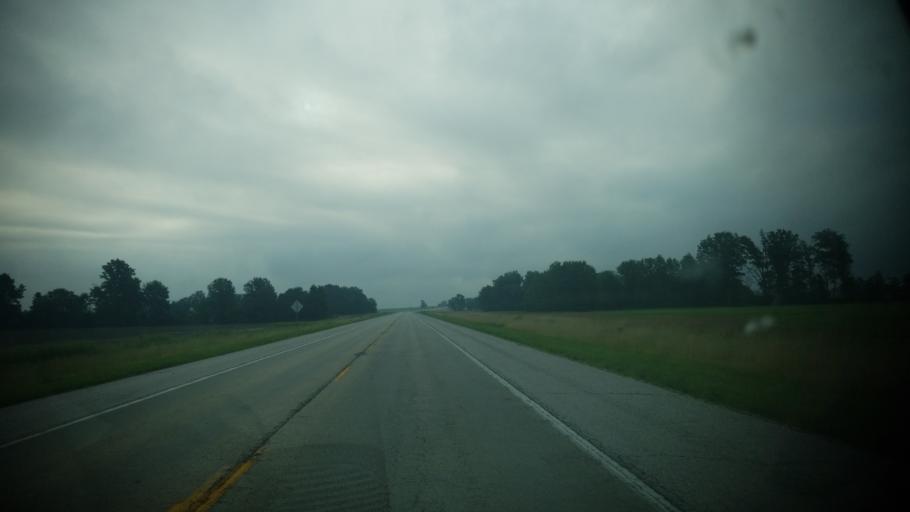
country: US
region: Illinois
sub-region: Clay County
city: Flora
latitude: 38.6759
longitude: -88.4269
